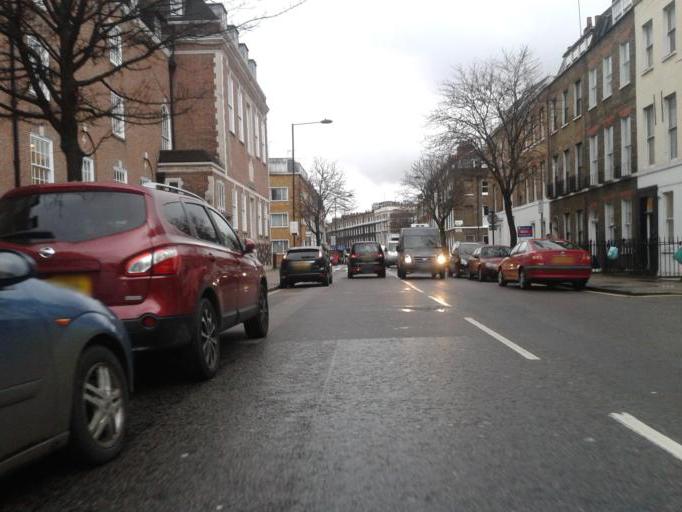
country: GB
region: England
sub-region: Greater London
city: Clerkenwell
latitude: 51.5241
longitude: -0.1181
